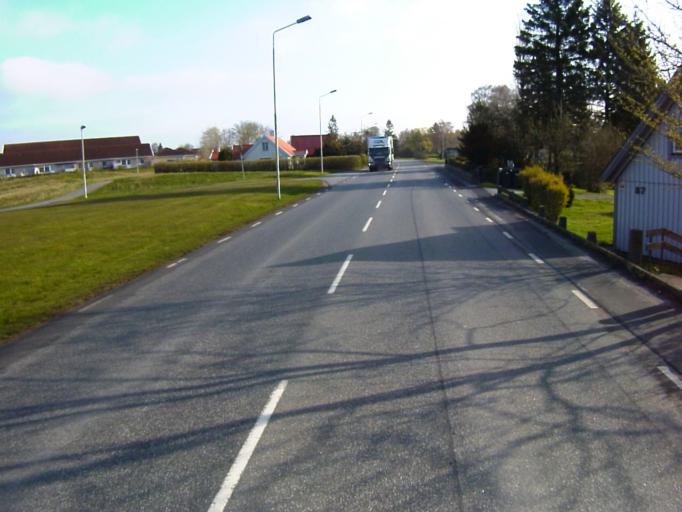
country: SE
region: Skane
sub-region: Kristianstads Kommun
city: Kristianstad
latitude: 56.0134
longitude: 14.1036
